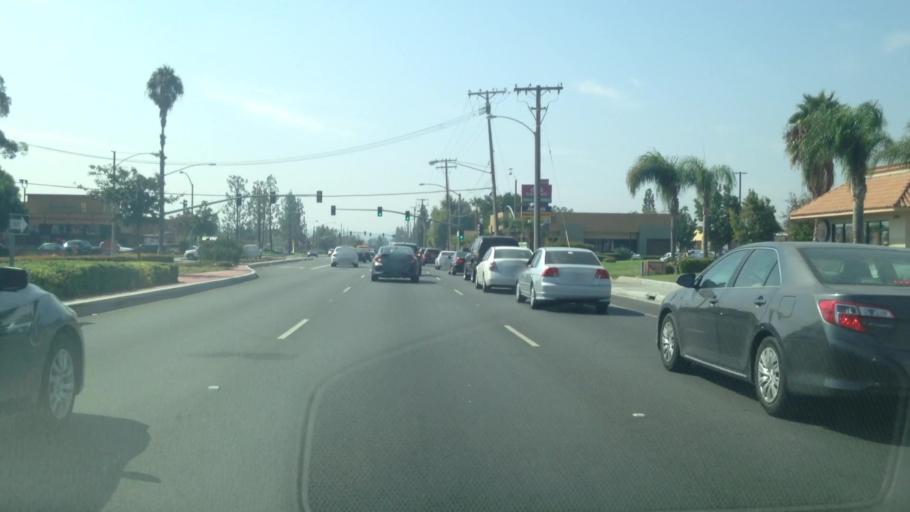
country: US
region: California
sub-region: Riverside County
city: Pedley
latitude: 33.9420
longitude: -117.4541
